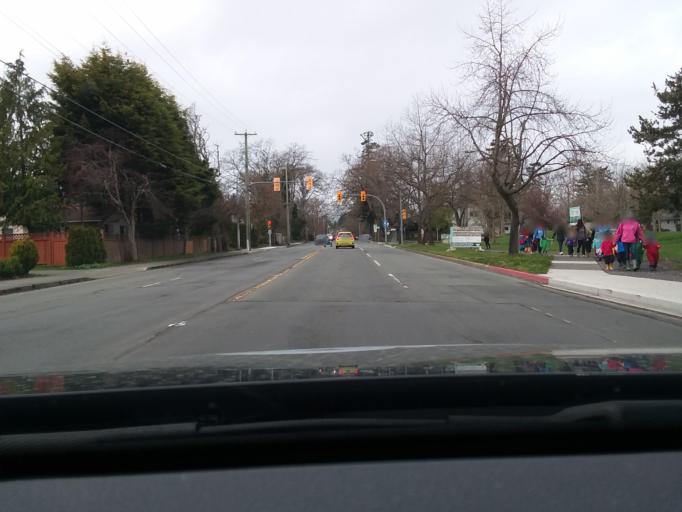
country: CA
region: British Columbia
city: Oak Bay
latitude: 48.4760
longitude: -123.3268
